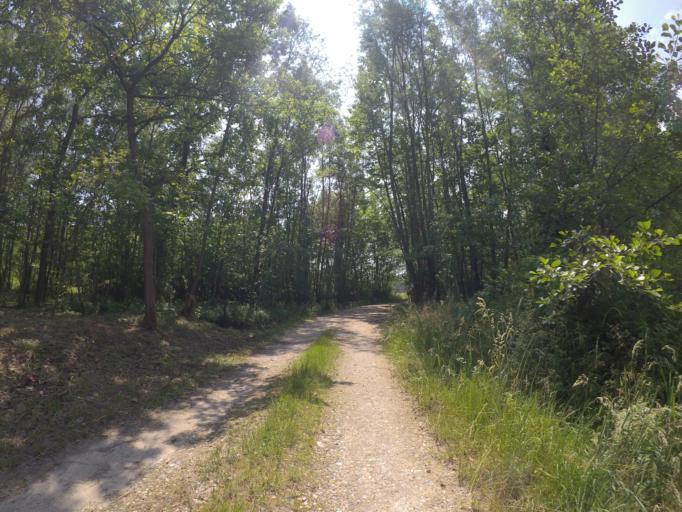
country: IT
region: Friuli Venezia Giulia
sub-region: Provincia di Udine
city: Bertiolo
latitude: 45.9169
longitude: 13.0352
